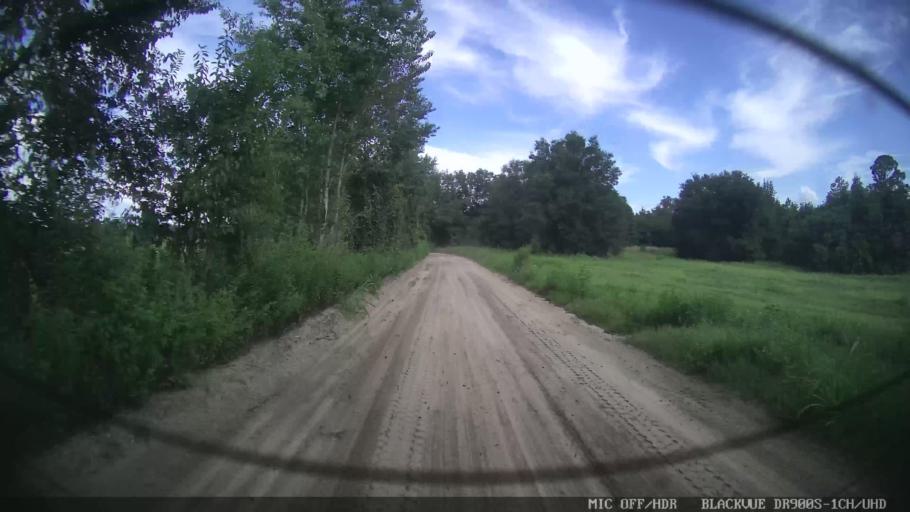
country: US
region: Florida
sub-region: Madison County
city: Madison
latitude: 30.5846
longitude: -83.2228
